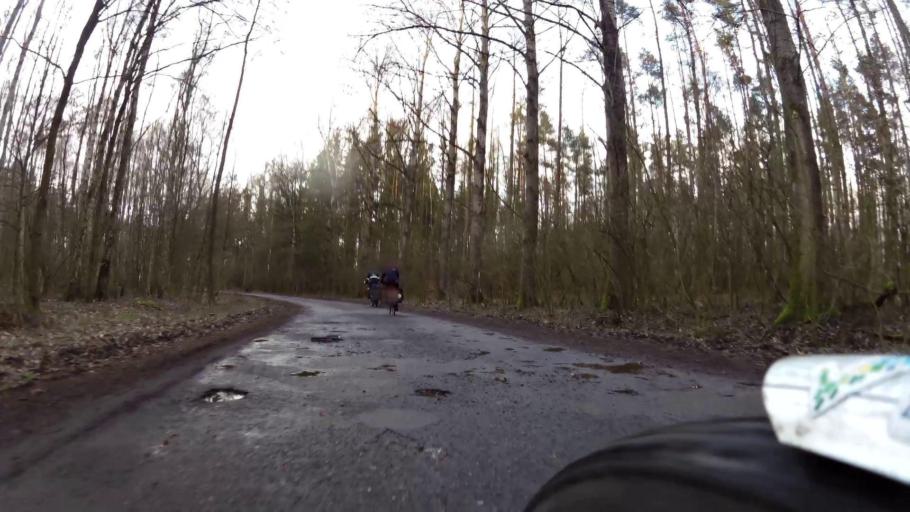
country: PL
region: West Pomeranian Voivodeship
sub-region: Powiat kamienski
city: Kamien Pomorski
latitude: 53.9077
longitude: 14.7329
